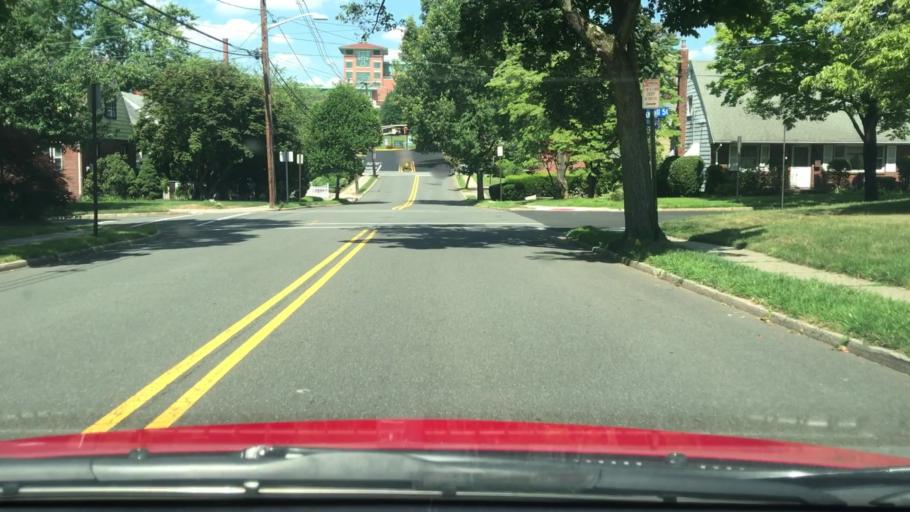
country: US
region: New Jersey
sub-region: Bergen County
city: Teaneck
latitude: 40.8819
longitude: -74.0073
